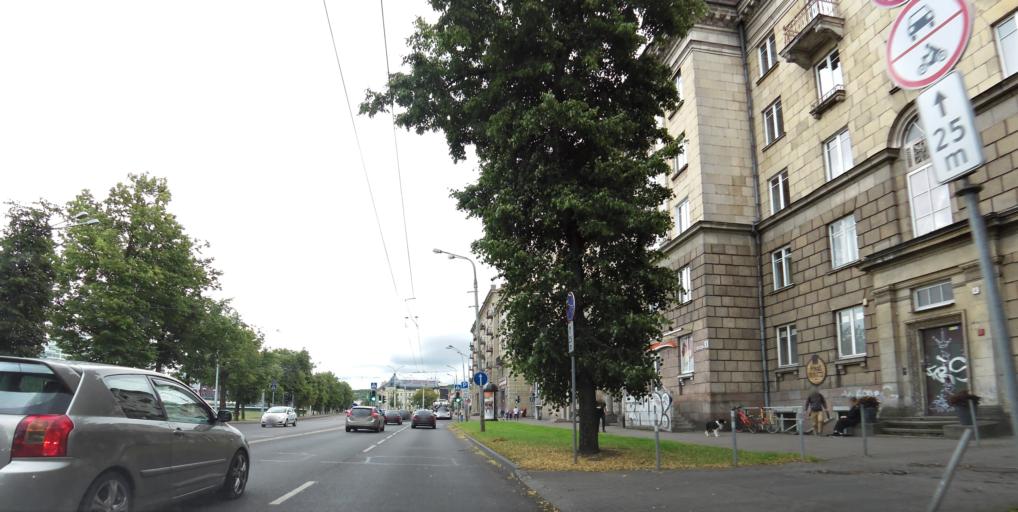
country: LT
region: Vilnius County
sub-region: Vilnius
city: Vilnius
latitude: 54.6912
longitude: 25.2754
